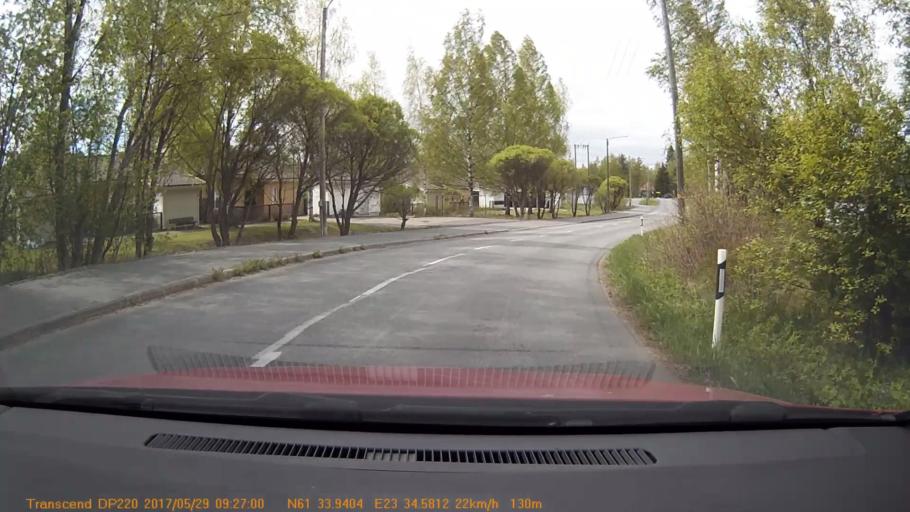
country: FI
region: Pirkanmaa
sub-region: Tampere
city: Yloejaervi
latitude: 61.5657
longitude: 23.5764
